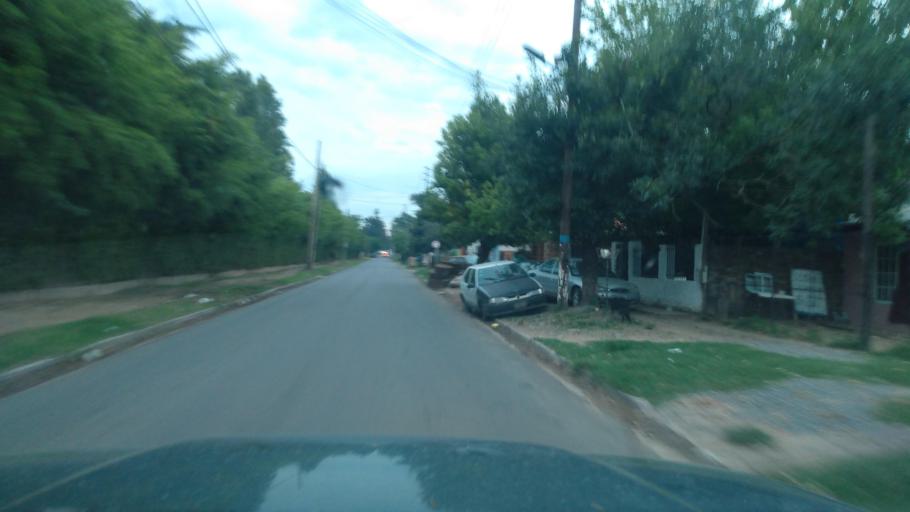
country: AR
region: Buenos Aires
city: Hurlingham
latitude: -34.5677
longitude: -58.7138
